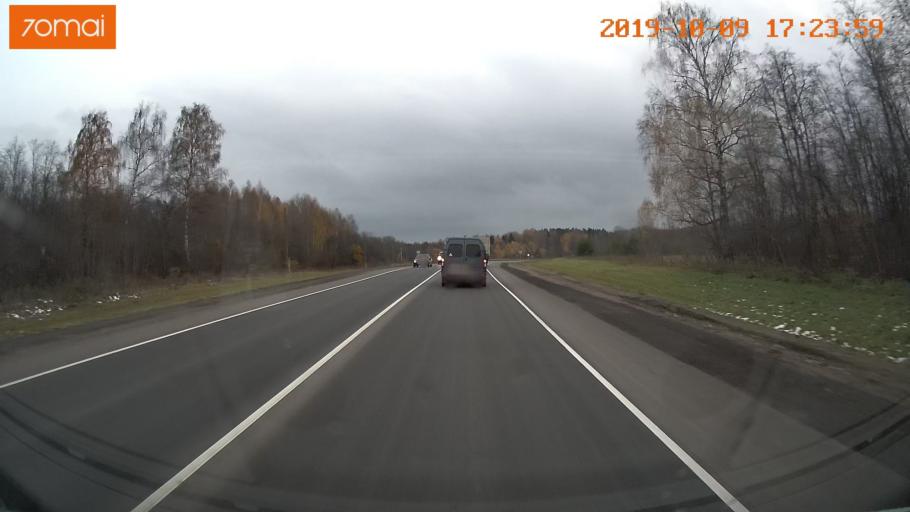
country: RU
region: Ivanovo
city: Furmanov
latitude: 57.1893
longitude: 41.1122
